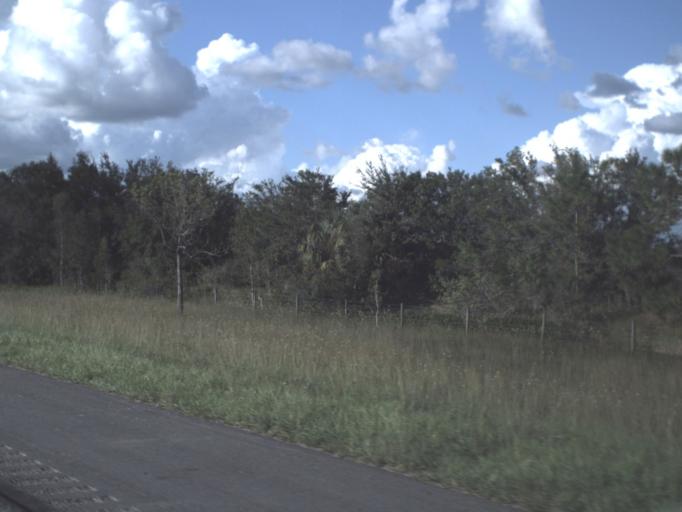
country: US
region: Florida
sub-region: Lee County
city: Suncoast Estates
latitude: 26.7876
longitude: -81.9013
